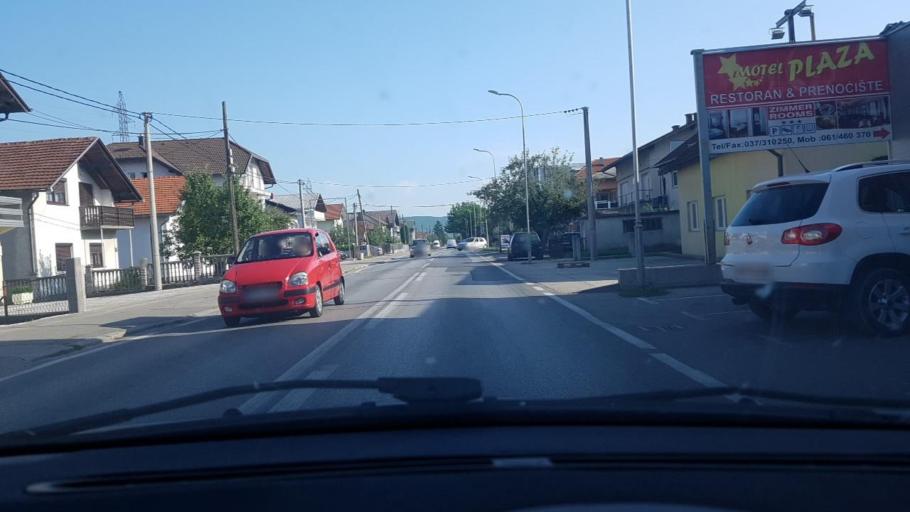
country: BA
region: Federation of Bosnia and Herzegovina
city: Bihac
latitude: 44.8242
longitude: 15.8817
